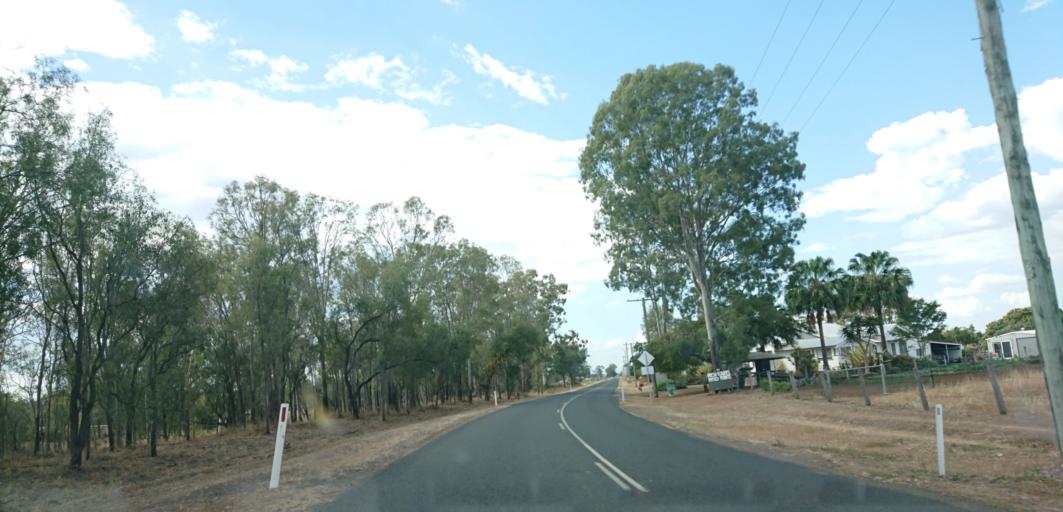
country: AU
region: Queensland
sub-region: Lockyer Valley
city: Gatton
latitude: -27.6072
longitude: 152.2099
